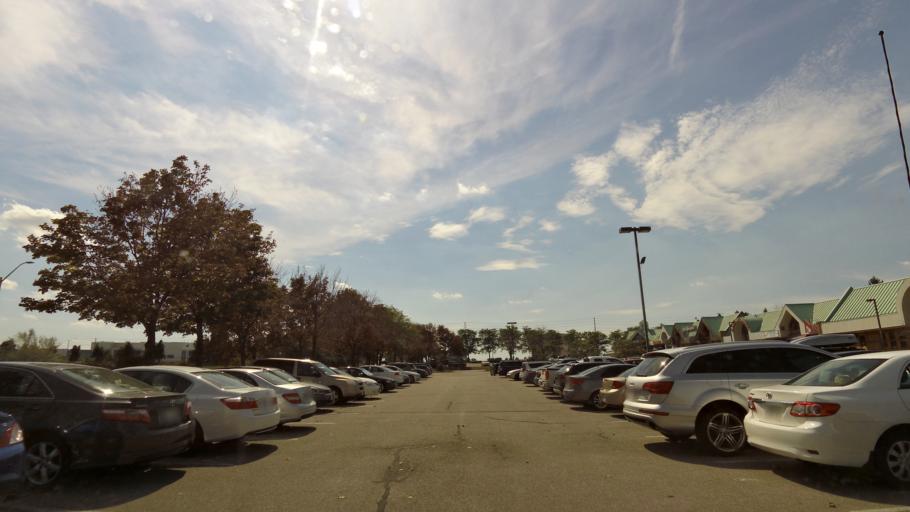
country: CA
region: Ontario
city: Mississauga
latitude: 43.6262
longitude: -79.6761
